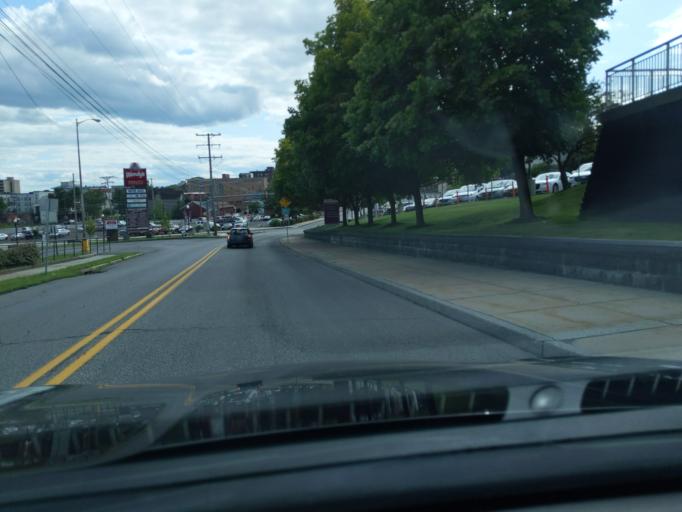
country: US
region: Pennsylvania
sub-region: Blair County
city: Altoona
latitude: 40.5215
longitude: -78.3979
